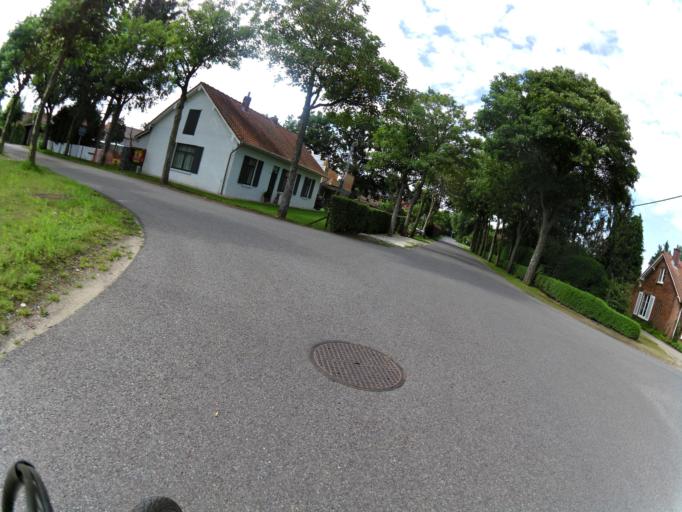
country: BE
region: Flanders
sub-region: Provincie Antwerpen
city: Balen
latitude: 51.1928
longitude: 5.2170
